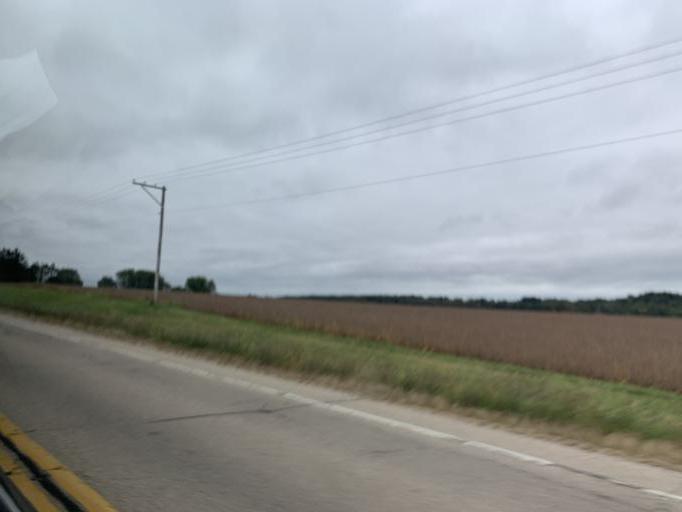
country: US
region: Wisconsin
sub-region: Grant County
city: Muscoda
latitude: 43.2198
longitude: -90.5262
